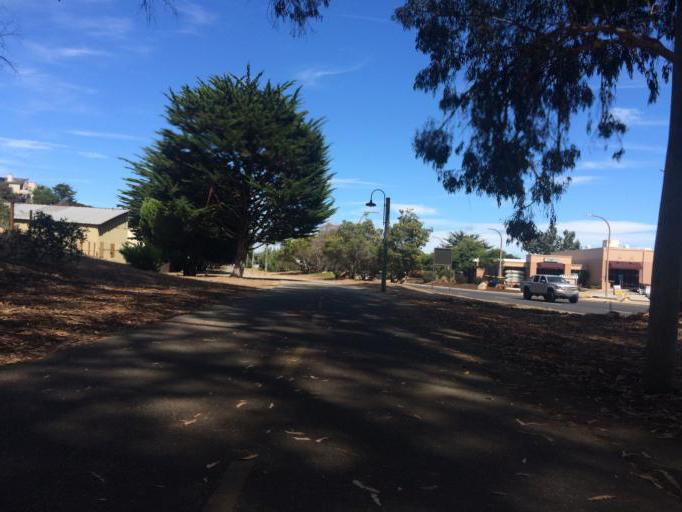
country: US
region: California
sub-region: Monterey County
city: Seaside
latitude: 36.6009
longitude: -121.8695
